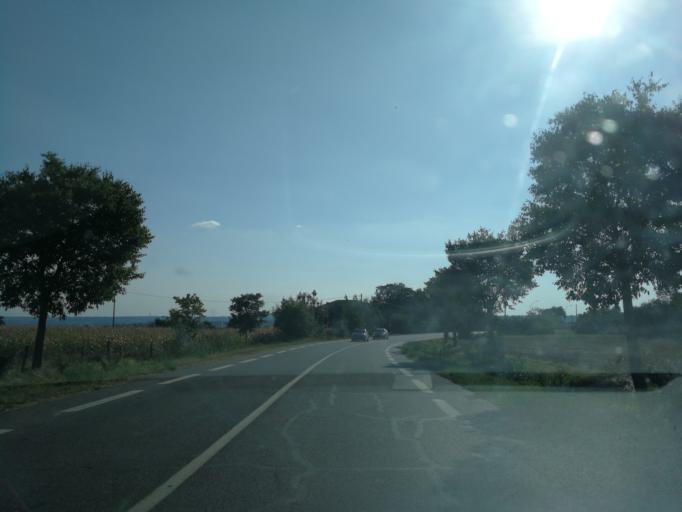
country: FR
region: Midi-Pyrenees
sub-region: Departement de la Haute-Garonne
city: Balma
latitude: 43.6106
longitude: 1.5235
